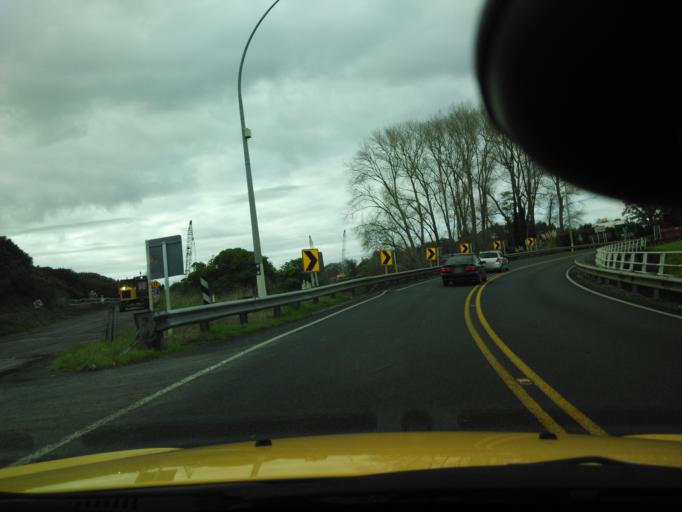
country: NZ
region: Waikato
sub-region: Waikato District
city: Ngaruawahia
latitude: -37.6086
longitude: 175.1846
